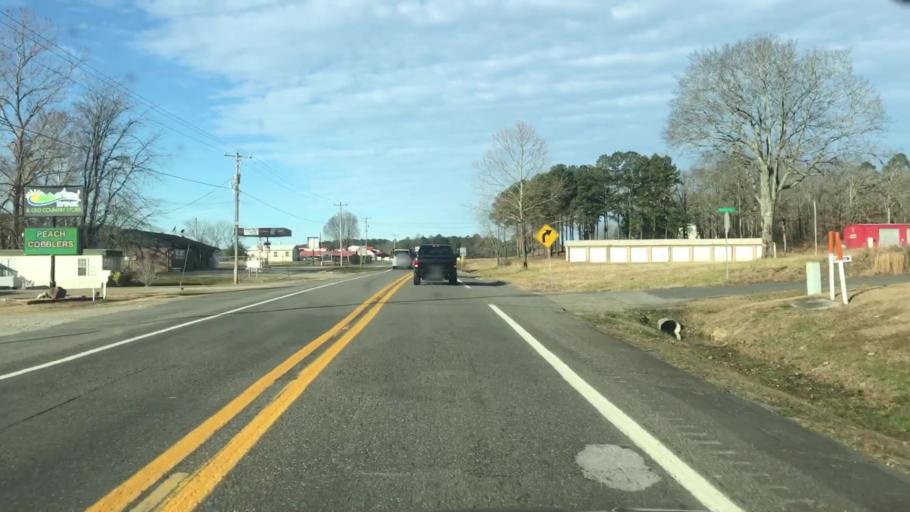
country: US
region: Arkansas
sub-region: Montgomery County
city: Mount Ida
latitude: 34.5311
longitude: -93.5266
